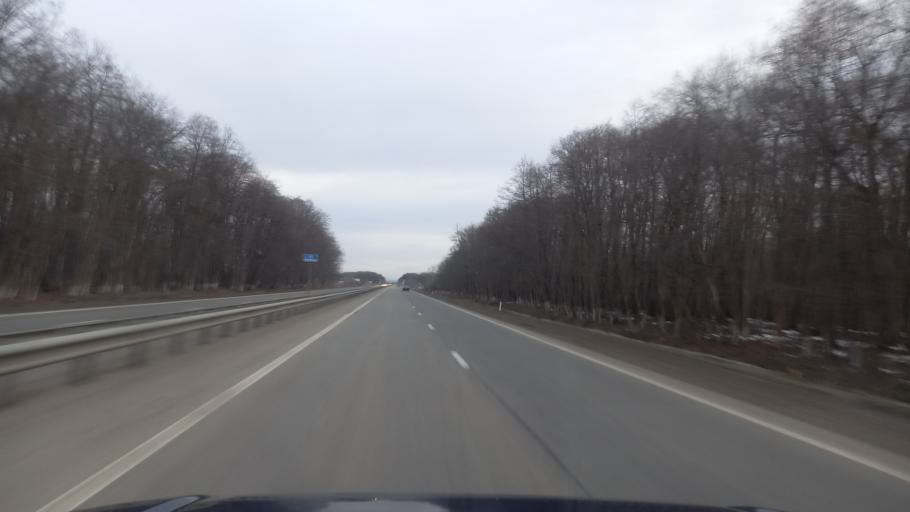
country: RU
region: Adygeya
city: Khanskaya
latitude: 44.7305
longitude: 39.9455
